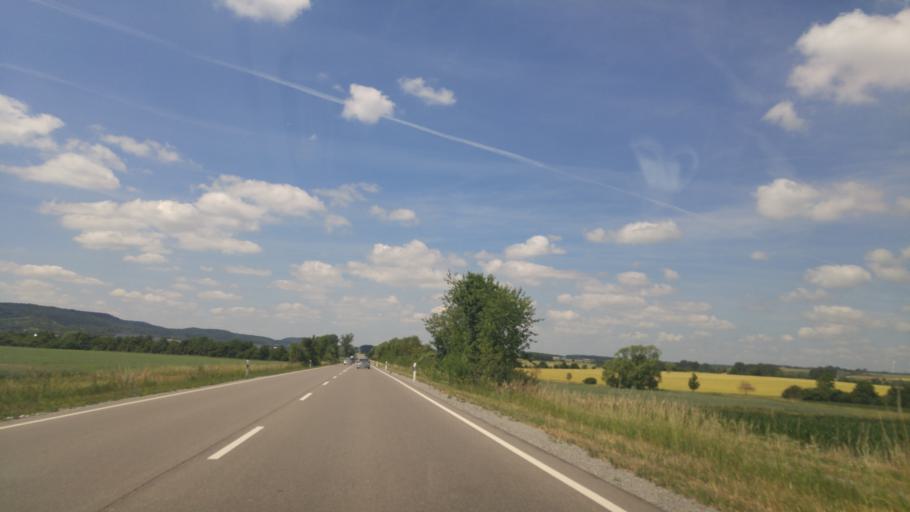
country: DE
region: Bavaria
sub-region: Regierungsbezirk Mittelfranken
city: Burgbernheim
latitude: 49.4674
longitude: 10.3454
